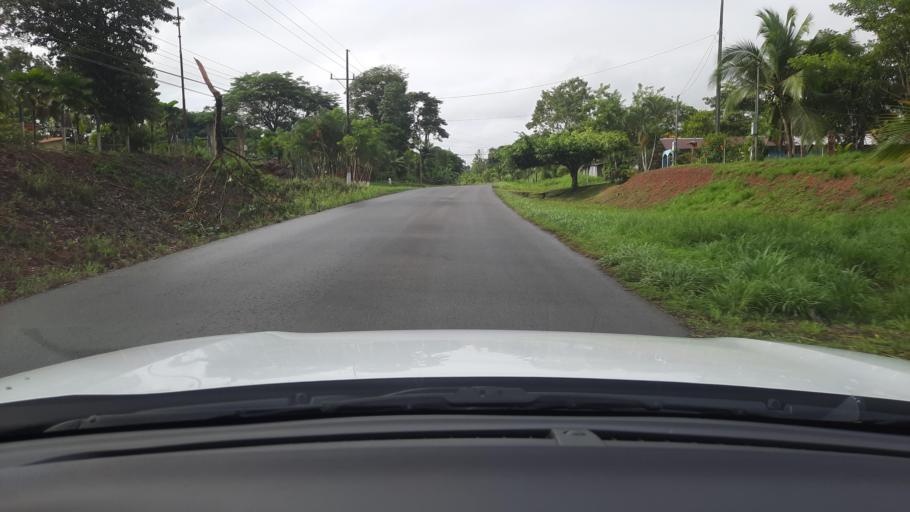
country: CR
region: Alajuela
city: San Jose
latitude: 10.9382
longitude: -85.1097
